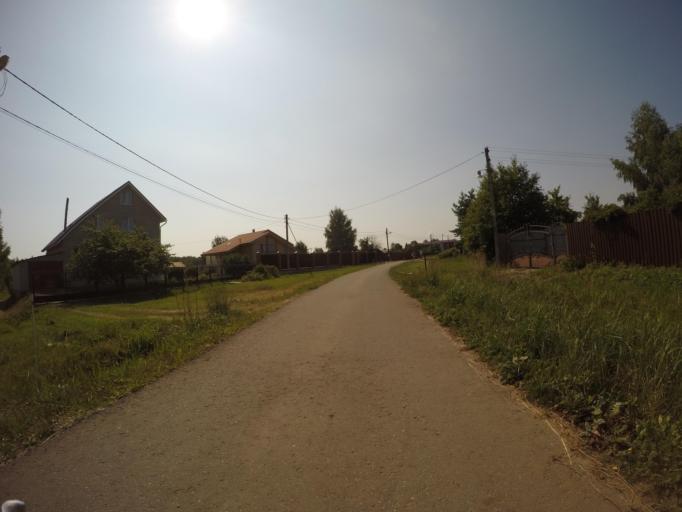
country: RU
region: Moskovskaya
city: Rechitsy
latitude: 55.6406
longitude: 38.5090
